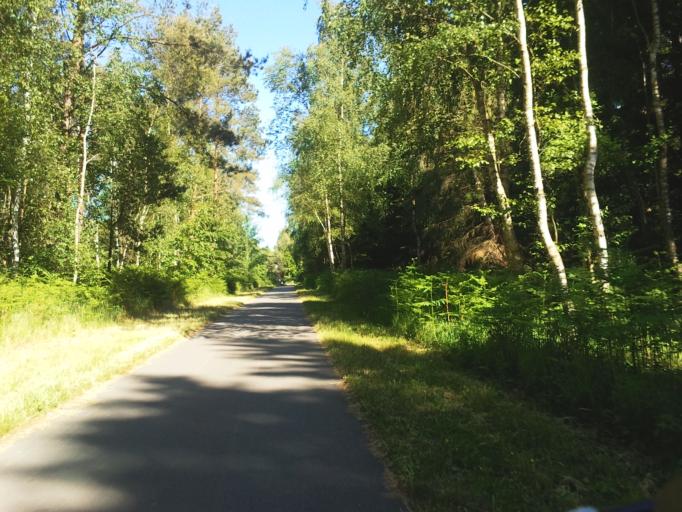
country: DE
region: Mecklenburg-Vorpommern
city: Nienhagen
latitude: 54.1917
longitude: 12.1769
